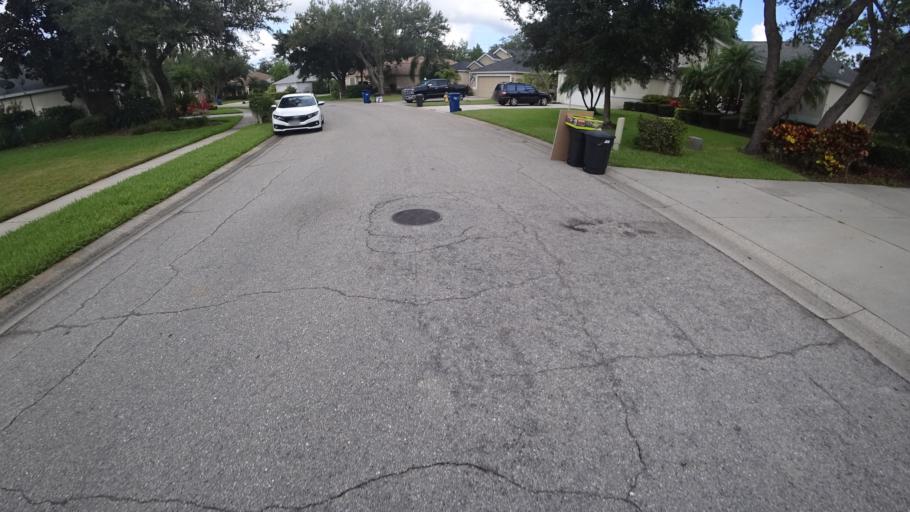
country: US
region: Florida
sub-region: Sarasota County
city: The Meadows
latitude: 27.4204
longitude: -82.4318
